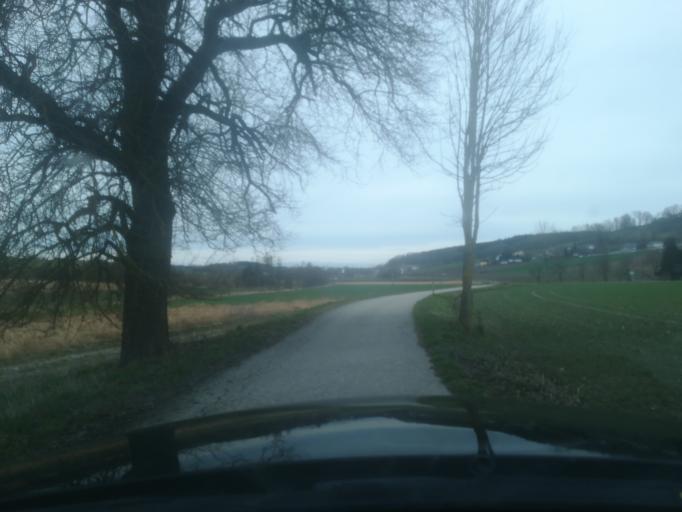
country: AT
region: Upper Austria
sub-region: Wels-Land
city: Neukirchen bei Lambach
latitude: 48.1026
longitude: 13.8216
